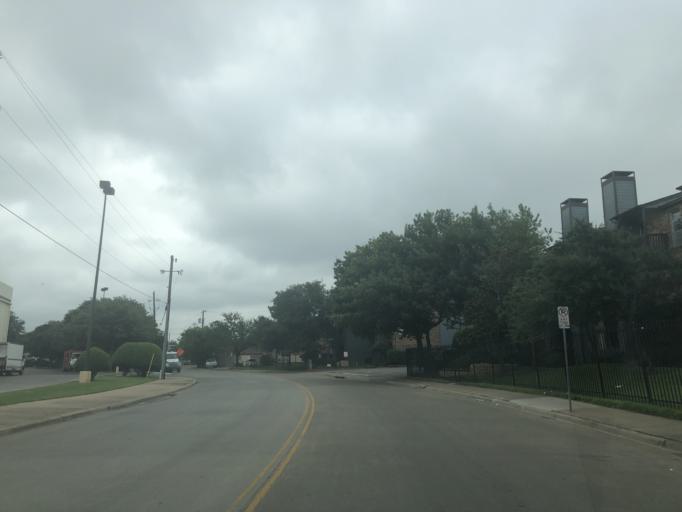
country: US
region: Texas
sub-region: Dallas County
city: University Park
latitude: 32.8635
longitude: -96.8635
